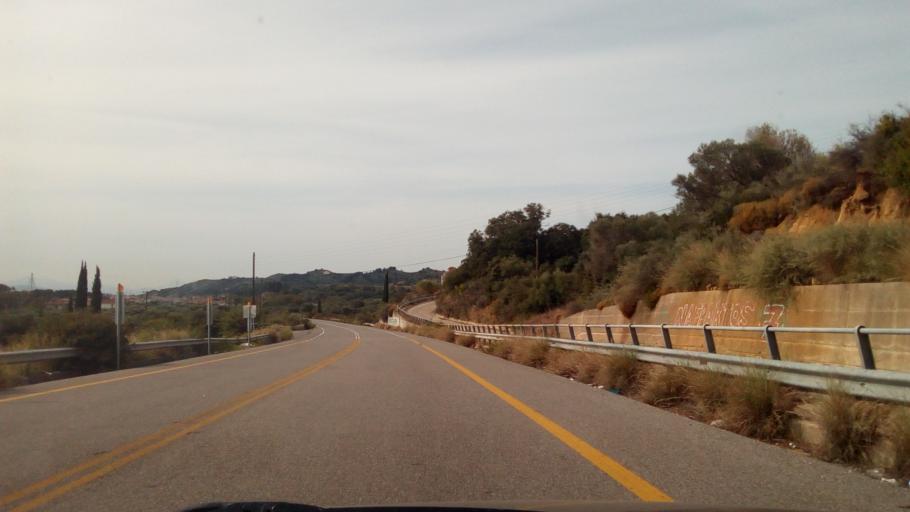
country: GR
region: West Greece
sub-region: Nomos Aitolias kai Akarnanias
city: Nafpaktos
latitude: 38.3759
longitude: 21.7838
